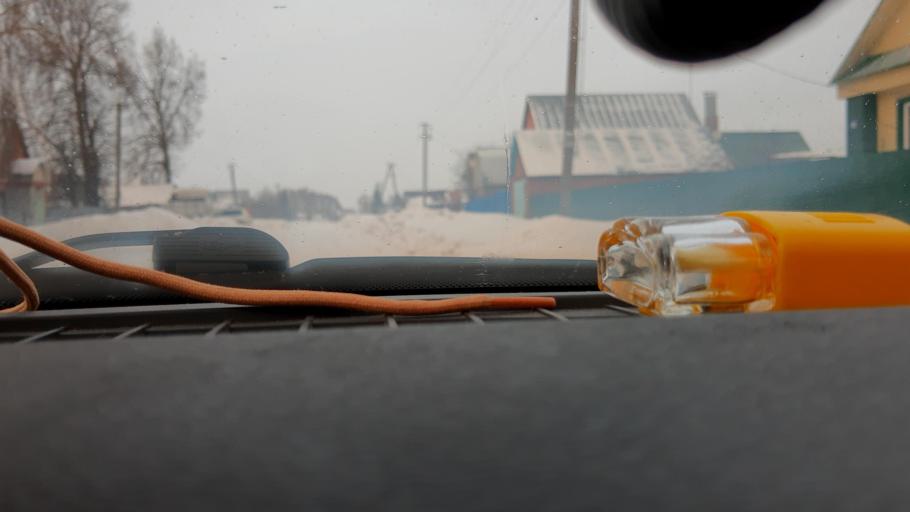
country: RU
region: Bashkortostan
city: Iglino
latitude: 54.7325
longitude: 56.3253
